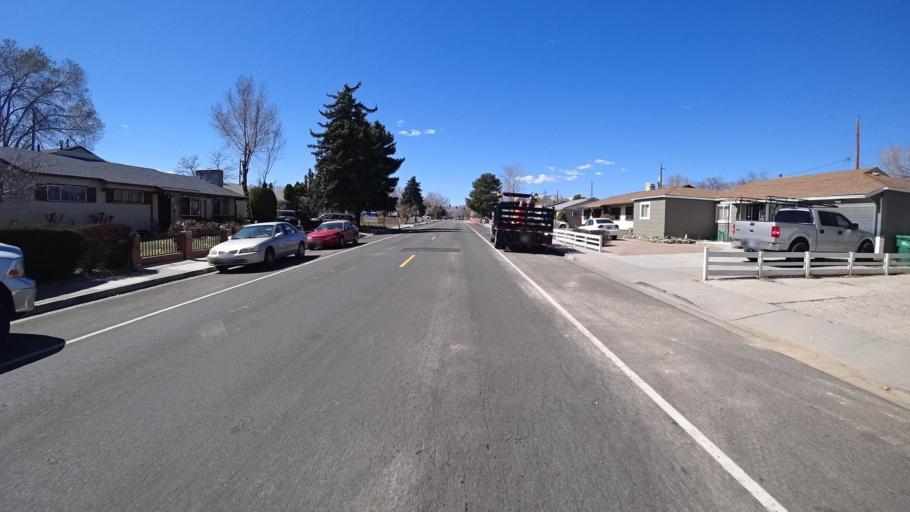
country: US
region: Nevada
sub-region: Washoe County
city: Sparks
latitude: 39.5529
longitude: -119.7599
